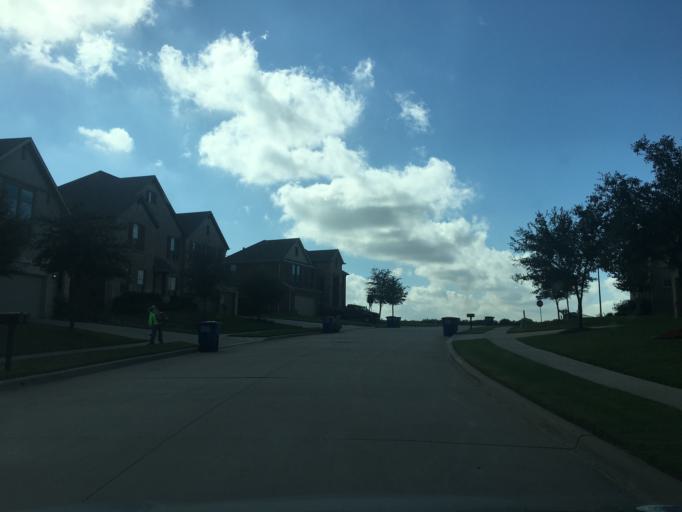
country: US
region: Texas
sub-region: Dallas County
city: Sachse
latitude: 32.9583
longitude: -96.5736
